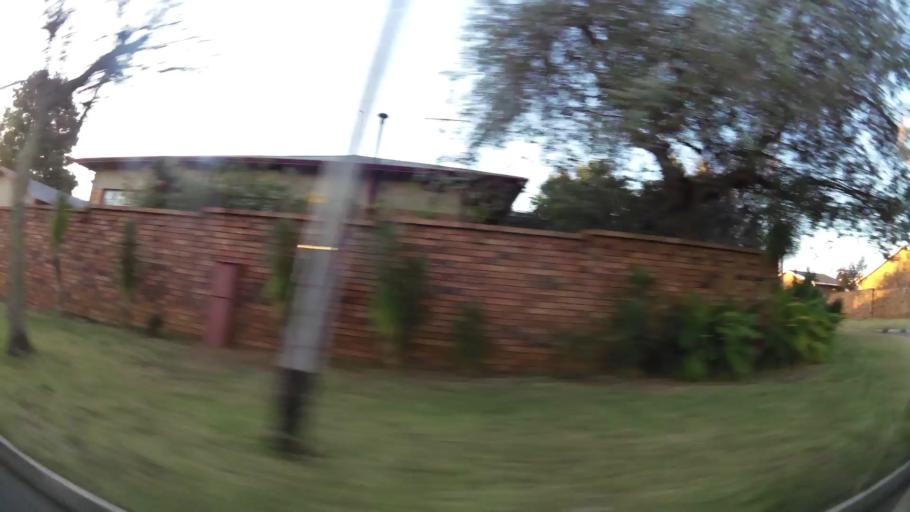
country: ZA
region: Gauteng
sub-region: City of Johannesburg Metropolitan Municipality
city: Roodepoort
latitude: -26.1572
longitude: 27.8893
